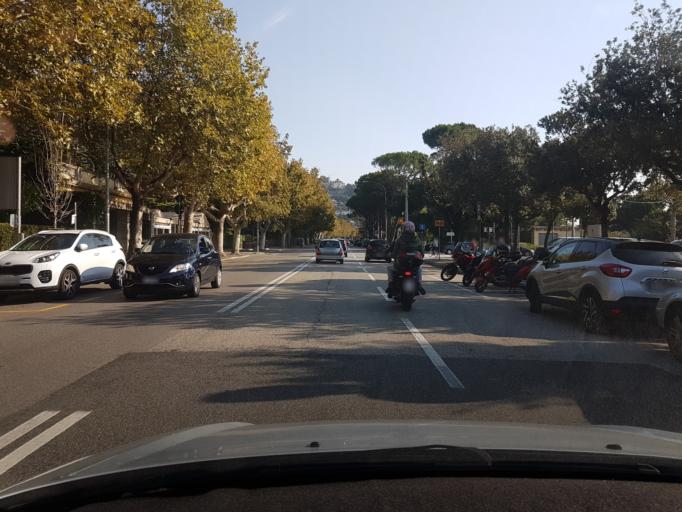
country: IT
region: Friuli Venezia Giulia
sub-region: Provincia di Trieste
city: Prosecco-Contovello
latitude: 45.6826
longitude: 13.7518
